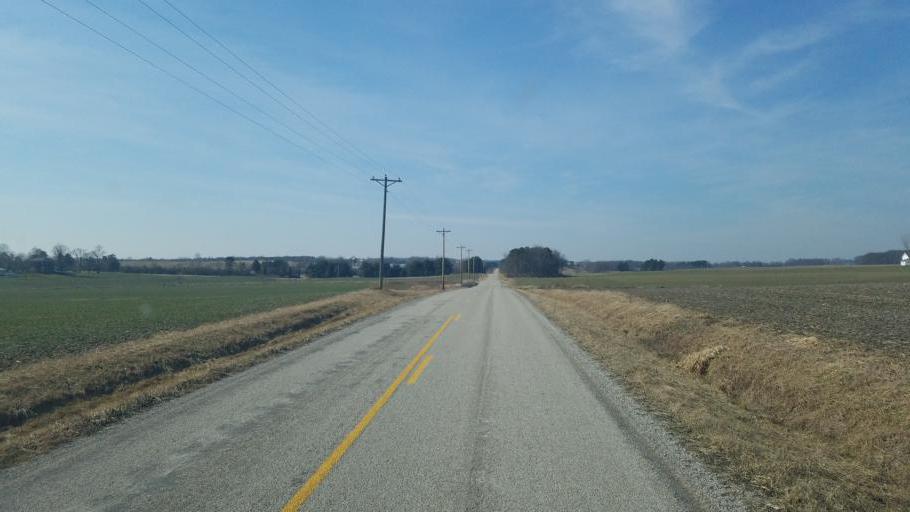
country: US
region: Ohio
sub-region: Ashland County
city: Ashland
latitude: 40.8060
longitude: -82.2434
